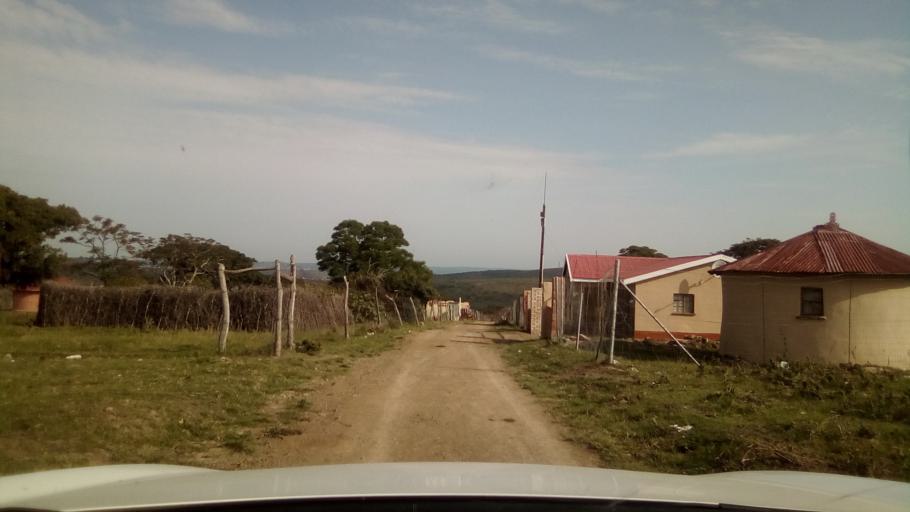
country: ZA
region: Eastern Cape
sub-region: Buffalo City Metropolitan Municipality
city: Bhisho
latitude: -33.0093
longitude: 27.3069
